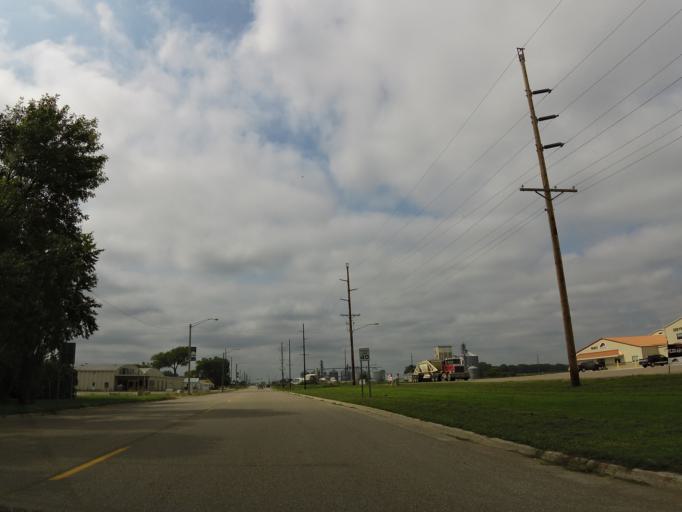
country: US
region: Minnesota
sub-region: Lac qui Parle County
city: Dawson
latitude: 44.9359
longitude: -96.0586
